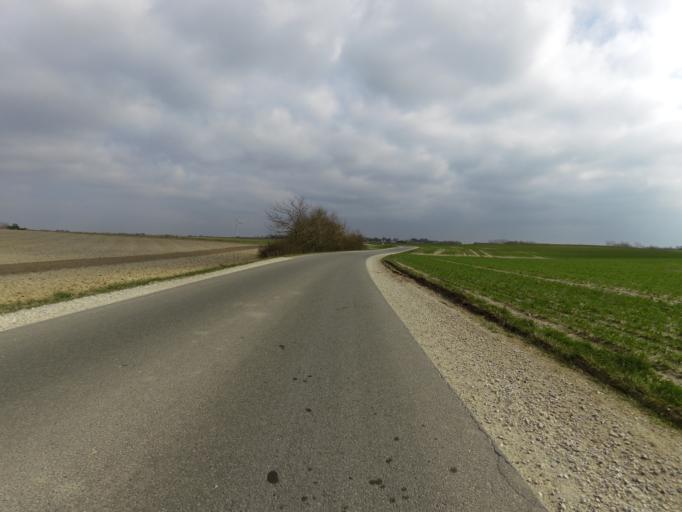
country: DK
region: Central Jutland
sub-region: Holstebro Kommune
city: Holstebro
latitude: 56.4340
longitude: 8.6755
